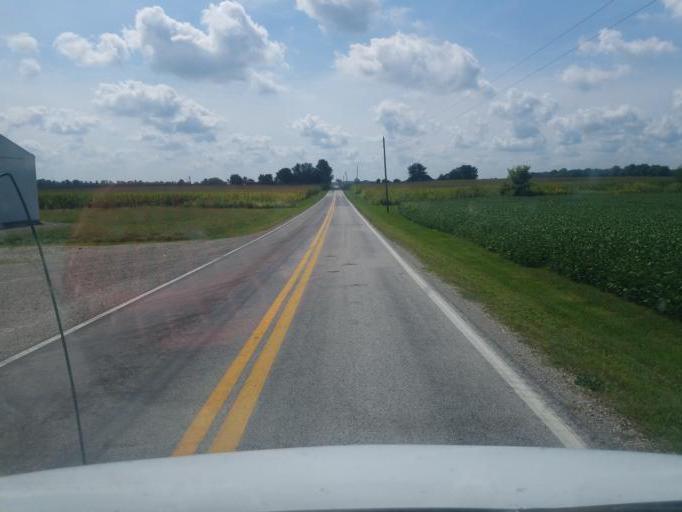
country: US
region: Ohio
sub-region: Marion County
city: Prospect
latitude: 40.4115
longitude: -83.1639
